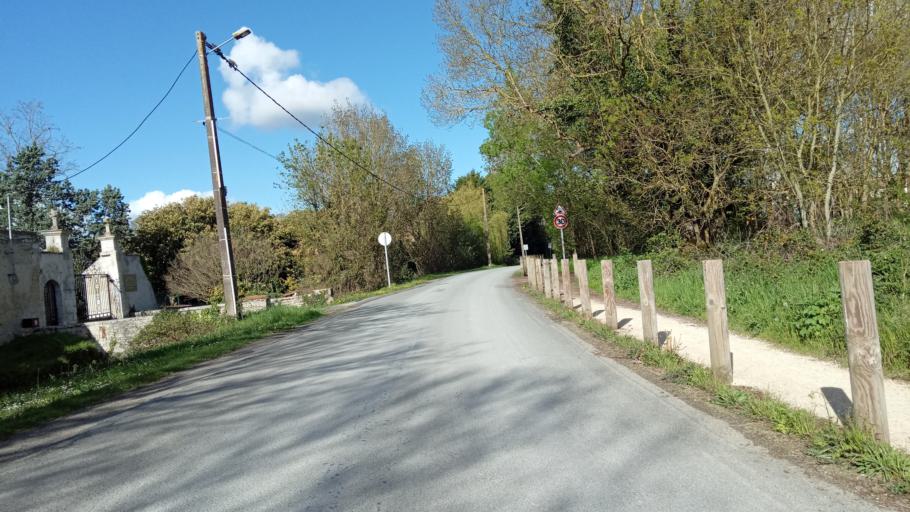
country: FR
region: Poitou-Charentes
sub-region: Departement de la Charente-Maritime
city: Verines
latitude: 46.1466
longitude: -0.9454
